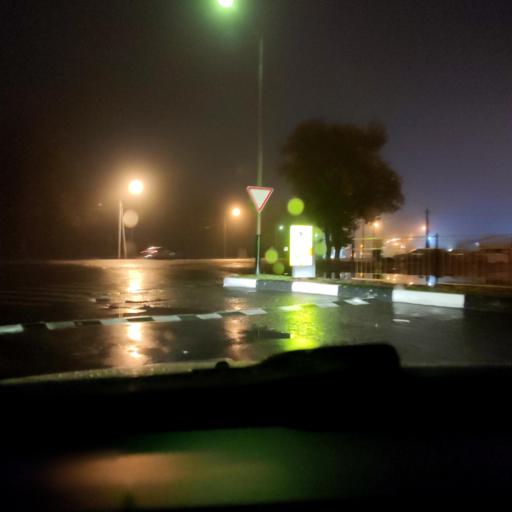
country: RU
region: Voronezj
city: Voronezh
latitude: 51.6196
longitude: 39.1760
